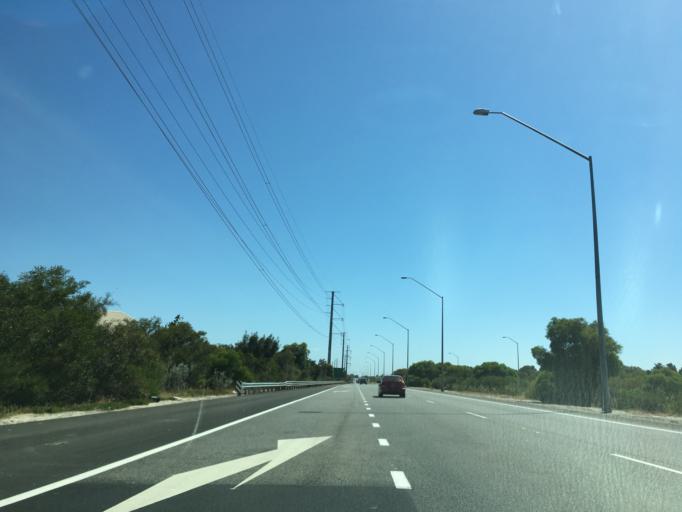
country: AU
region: Western Australia
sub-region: Canning
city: Willetton
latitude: -32.0601
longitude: 115.9013
